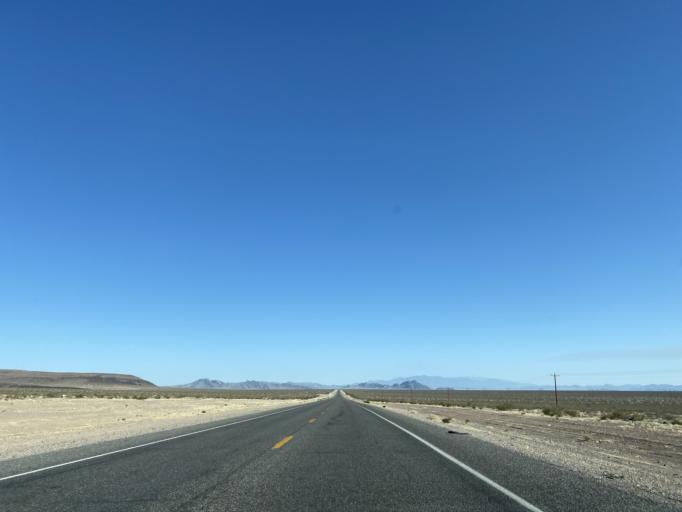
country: US
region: Nevada
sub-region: Nye County
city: Beatty
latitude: 36.6760
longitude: -116.5313
